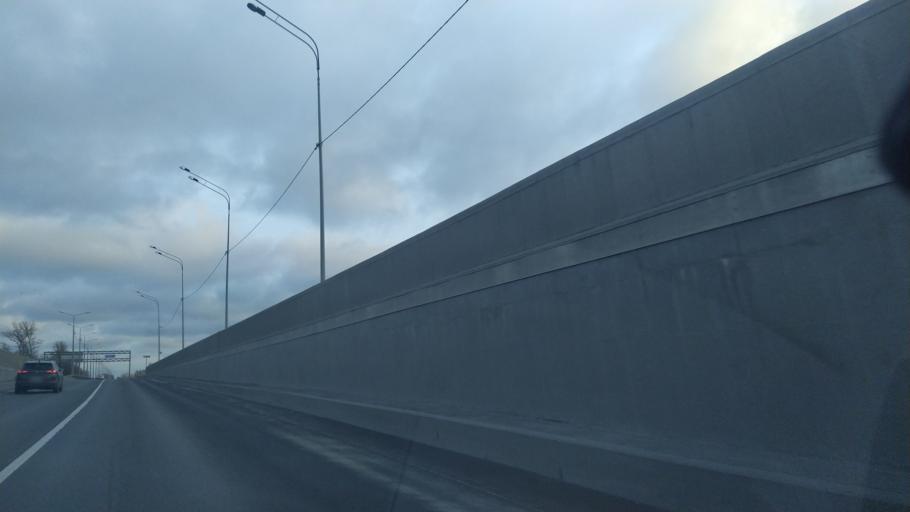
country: RU
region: St.-Petersburg
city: Aleksandrovskaya
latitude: 59.7765
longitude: 30.3276
